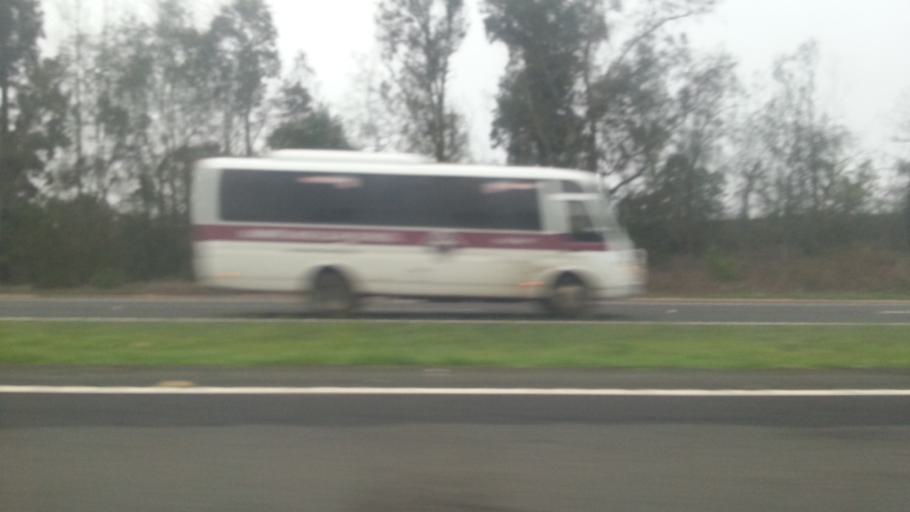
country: AU
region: New South Wales
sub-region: Camden
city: Elderslie
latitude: -34.0640
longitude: 150.7207
